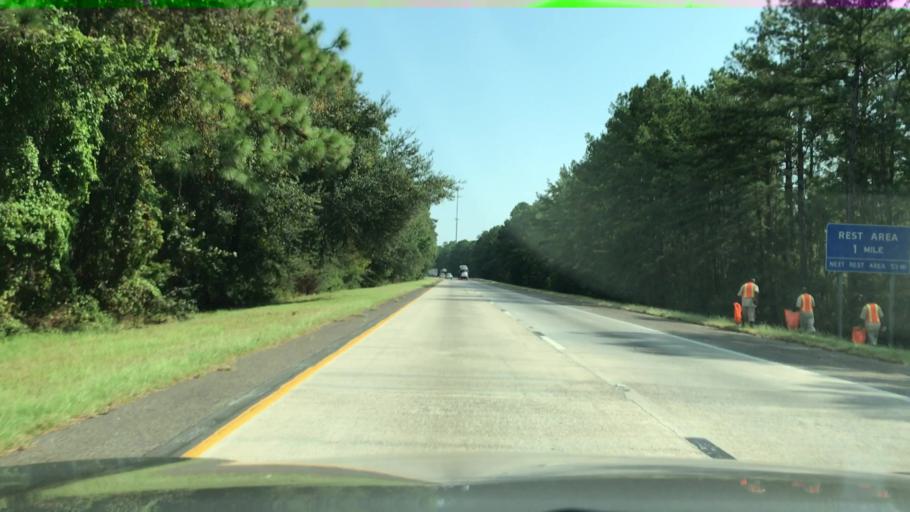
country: US
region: South Carolina
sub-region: Hampton County
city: Yemassee
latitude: 32.7880
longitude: -80.7807
